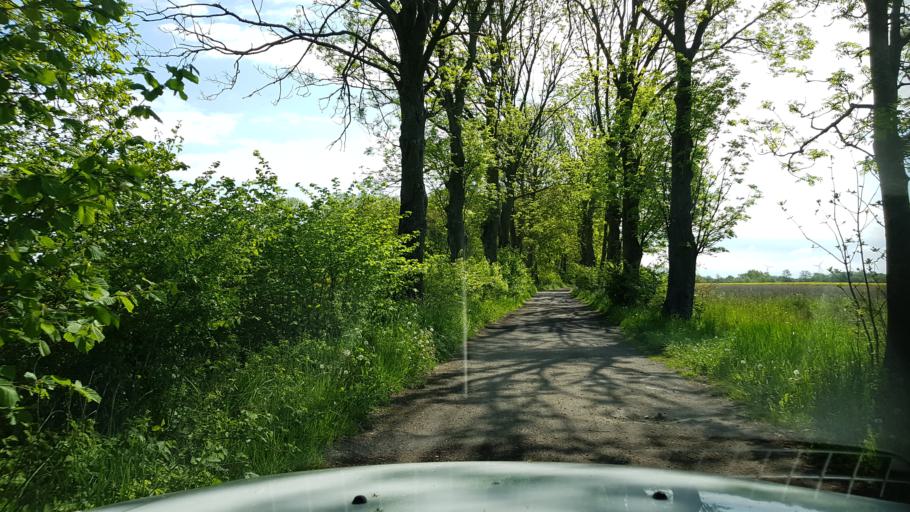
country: PL
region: West Pomeranian Voivodeship
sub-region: Powiat kolobrzeski
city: Ustronie Morskie
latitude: 54.2230
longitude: 15.8165
